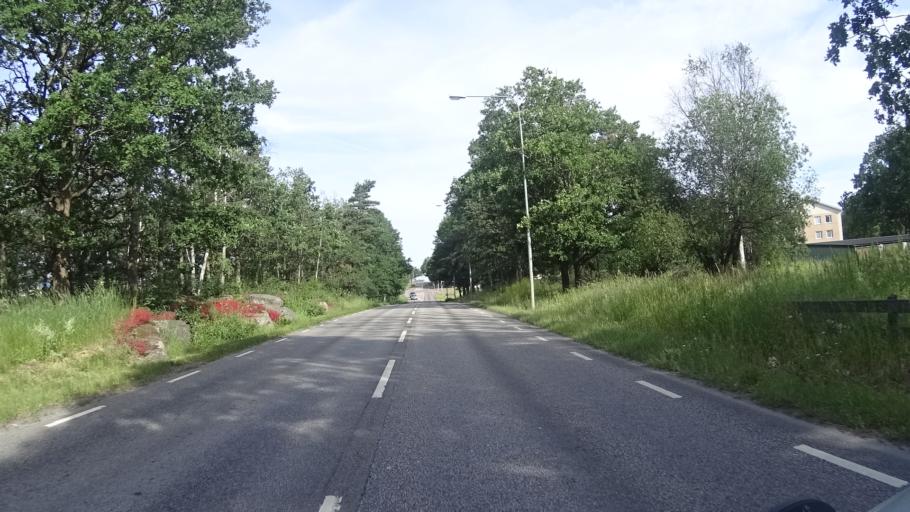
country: SE
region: Kalmar
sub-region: Oskarshamns Kommun
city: Oskarshamn
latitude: 57.2545
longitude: 16.4403
